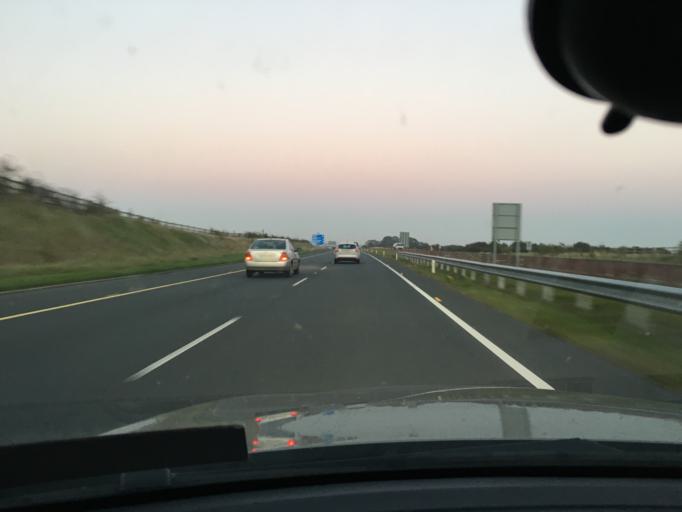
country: IE
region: Connaught
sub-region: County Galway
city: Oranmore
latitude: 53.2957
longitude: -8.9118
